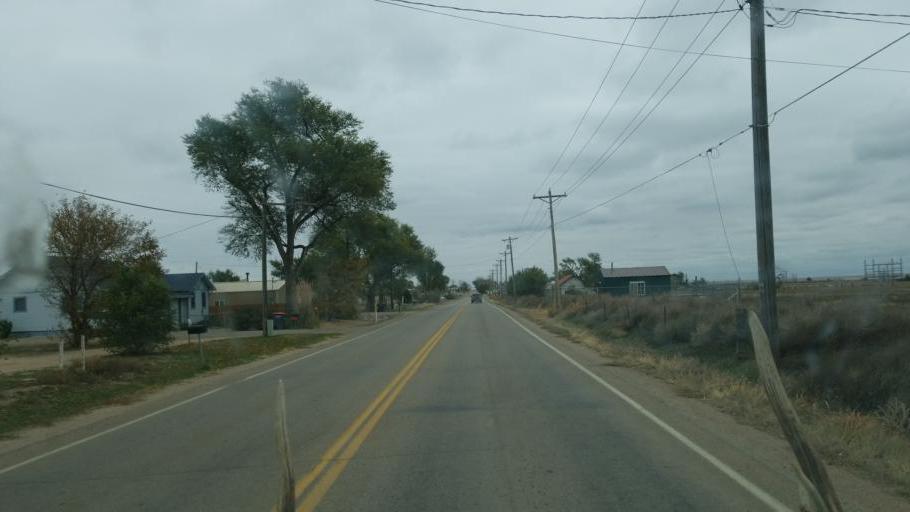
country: US
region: Colorado
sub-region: Crowley County
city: Ordway
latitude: 38.2145
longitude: -103.7523
